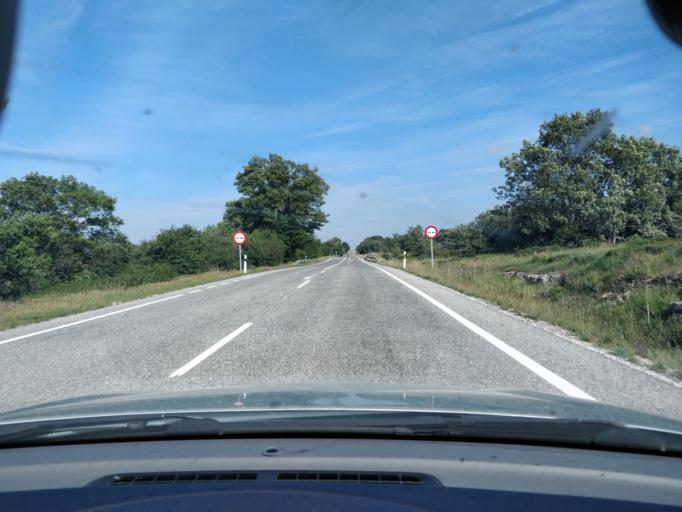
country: ES
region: Cantabria
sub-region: Provincia de Cantabria
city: San Martin de Elines
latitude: 42.9417
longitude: -3.7406
